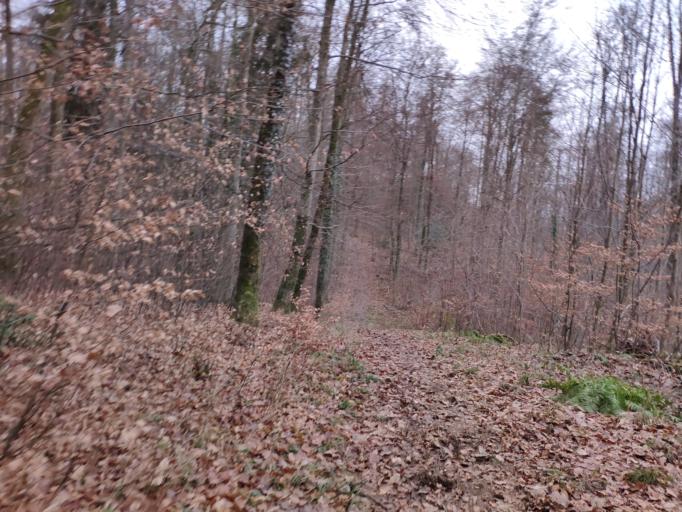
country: DE
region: Baden-Wuerttemberg
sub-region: Freiburg Region
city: Inzlingen
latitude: 47.5988
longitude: 7.6893
